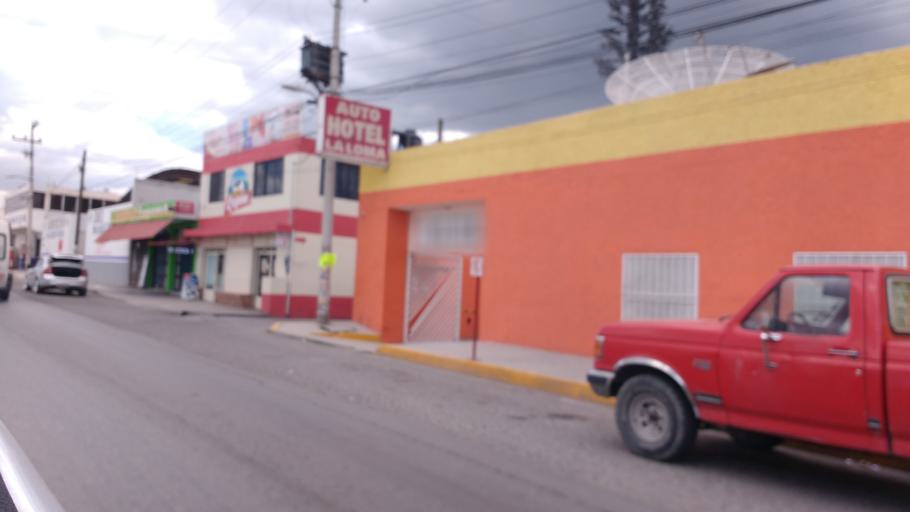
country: MX
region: Hidalgo
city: Tlahuelilpan
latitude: 20.1424
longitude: -99.2349
